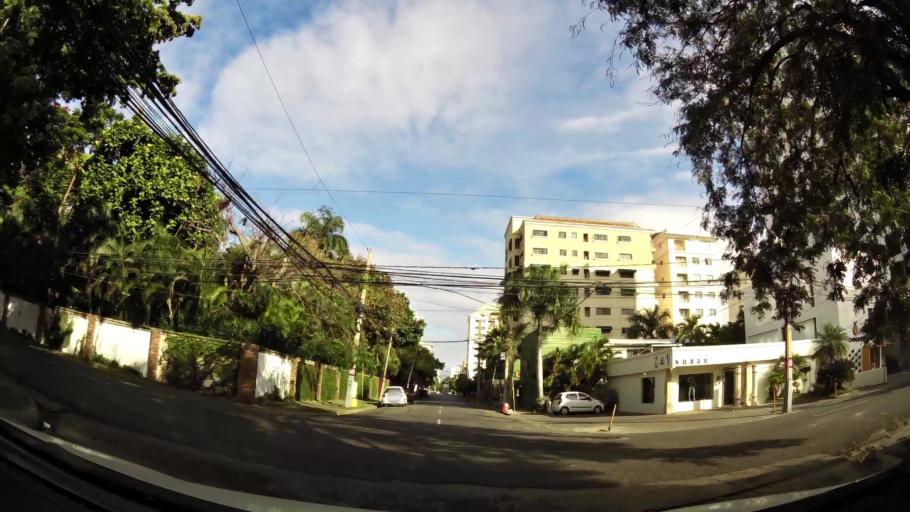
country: DO
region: Nacional
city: La Julia
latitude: 18.4708
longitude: -69.9358
